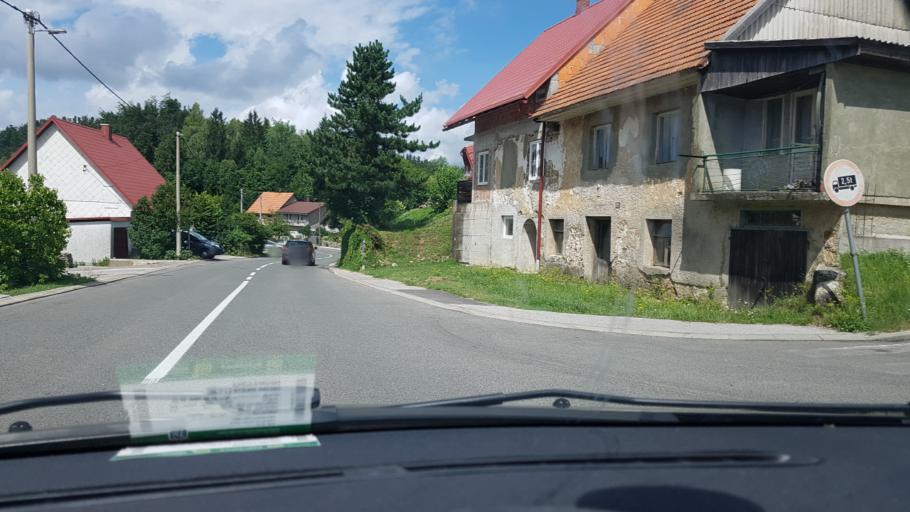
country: HR
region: Primorsko-Goranska
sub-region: Grad Delnice
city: Delnice
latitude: 45.3615
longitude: 14.7304
